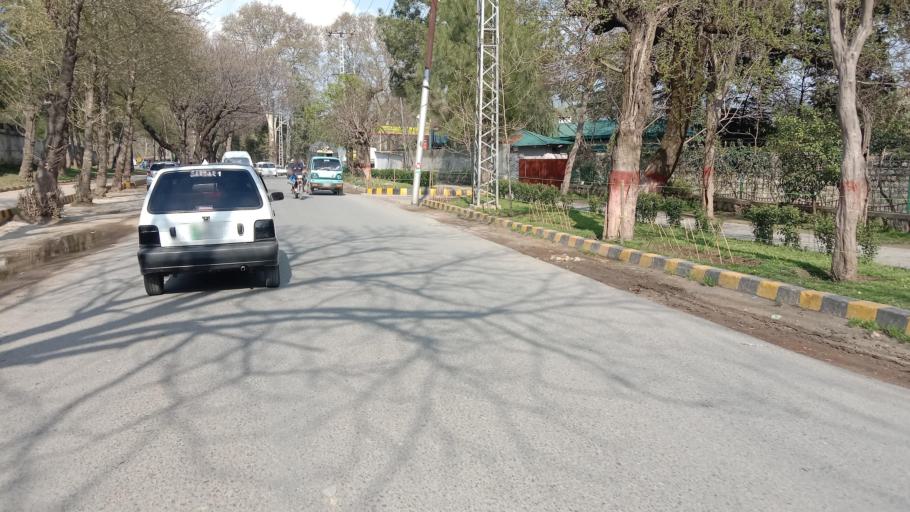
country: PK
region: Khyber Pakhtunkhwa
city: Abbottabad
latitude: 34.1512
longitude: 73.2160
